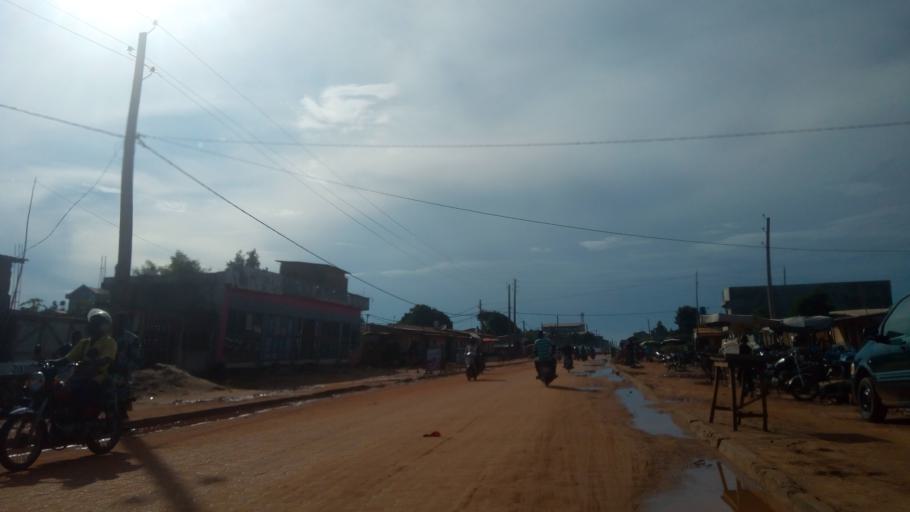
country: BJ
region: Atlantique
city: Abomey-Calavi
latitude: 6.4537
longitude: 2.3356
